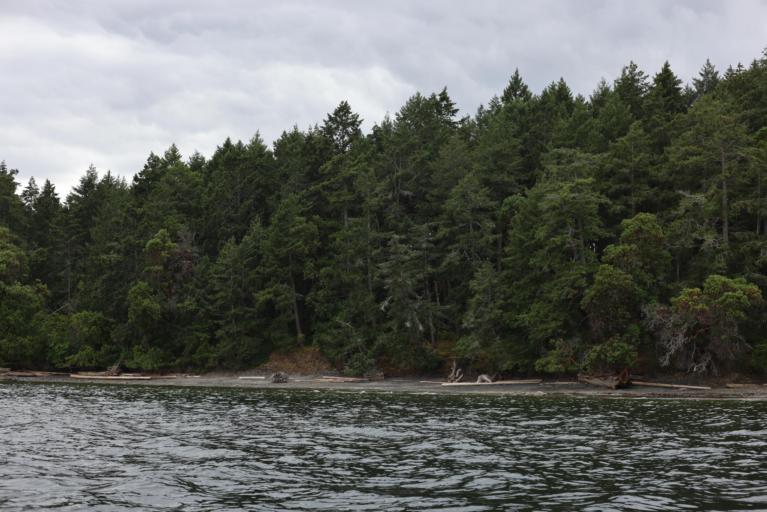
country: CA
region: British Columbia
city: North Cowichan
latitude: 48.9003
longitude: -123.6616
